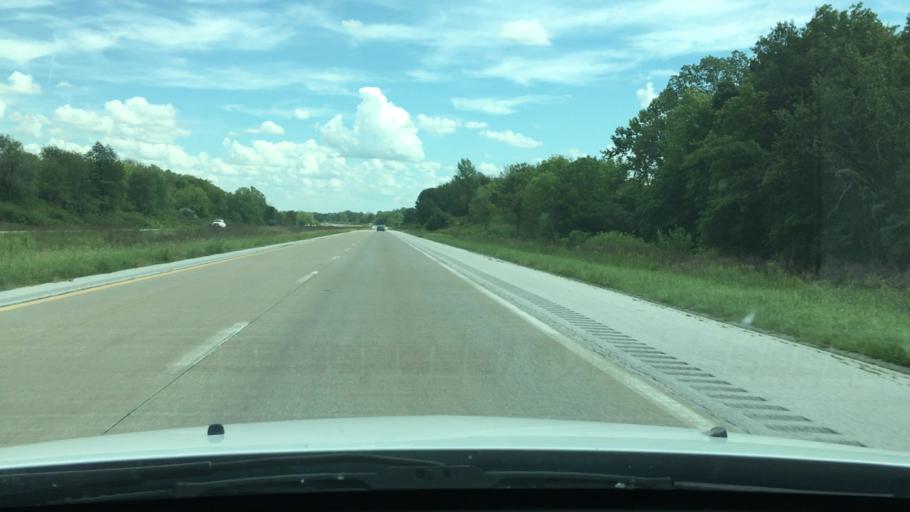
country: US
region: Illinois
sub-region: Scott County
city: Winchester
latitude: 39.6826
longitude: -90.5310
